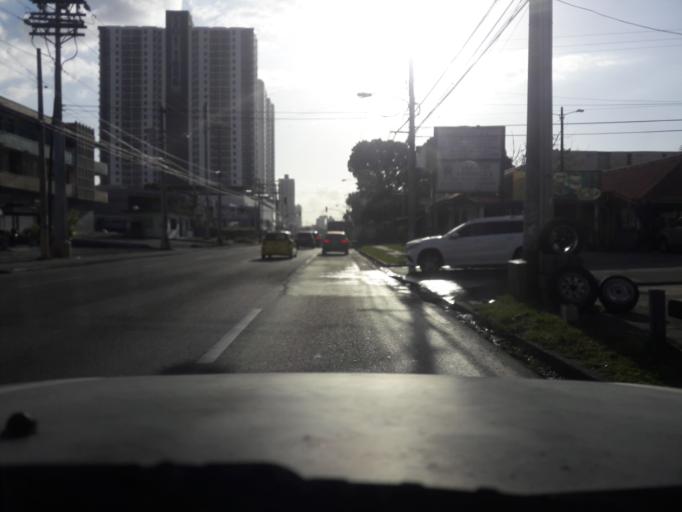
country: PA
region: Panama
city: Panama
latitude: 9.0179
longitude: -79.4939
